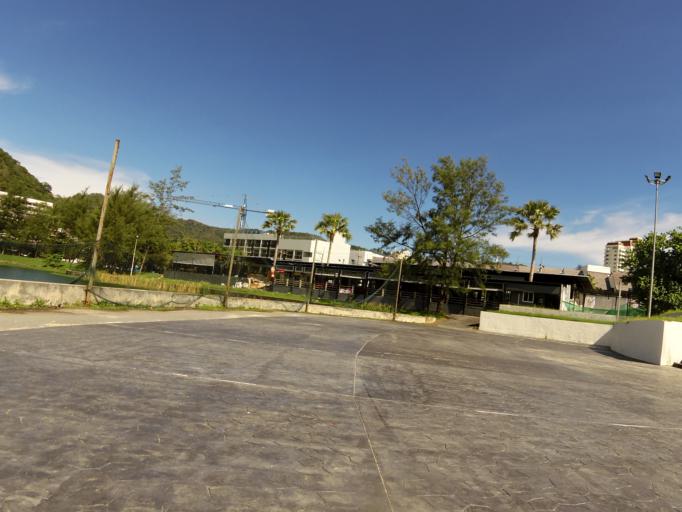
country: TH
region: Phuket
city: Ban Karon
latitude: 7.8514
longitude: 98.2931
